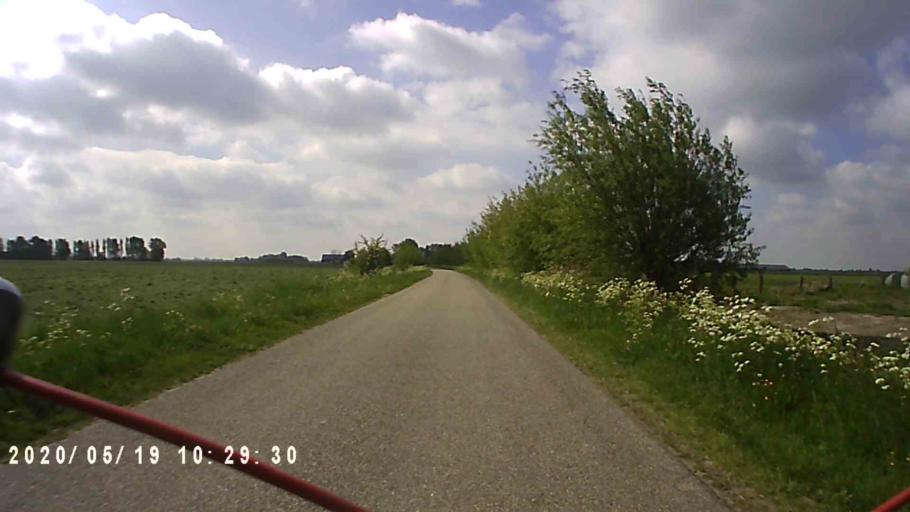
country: NL
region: Friesland
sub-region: Gemeente Kollumerland en Nieuwkruisland
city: Kollum
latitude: 53.2985
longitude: 6.1958
